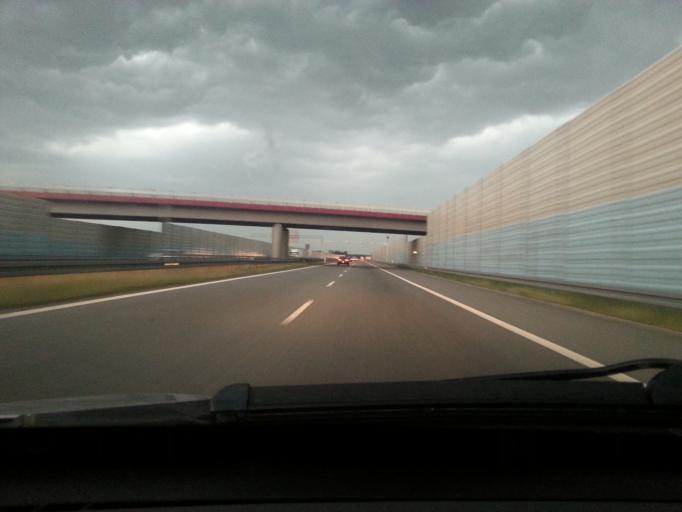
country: PL
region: Lodz Voivodeship
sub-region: powiat Lowicki
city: Lyszkowice
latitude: 51.9776
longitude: 19.8791
